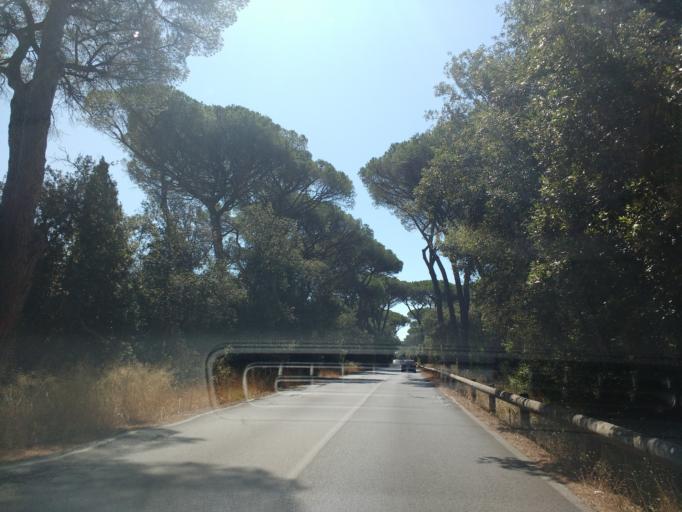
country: IT
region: Latium
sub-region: Citta metropolitana di Roma Capitale
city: Acilia-Castel Fusano-Ostia Antica
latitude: 41.7245
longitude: 12.3433
